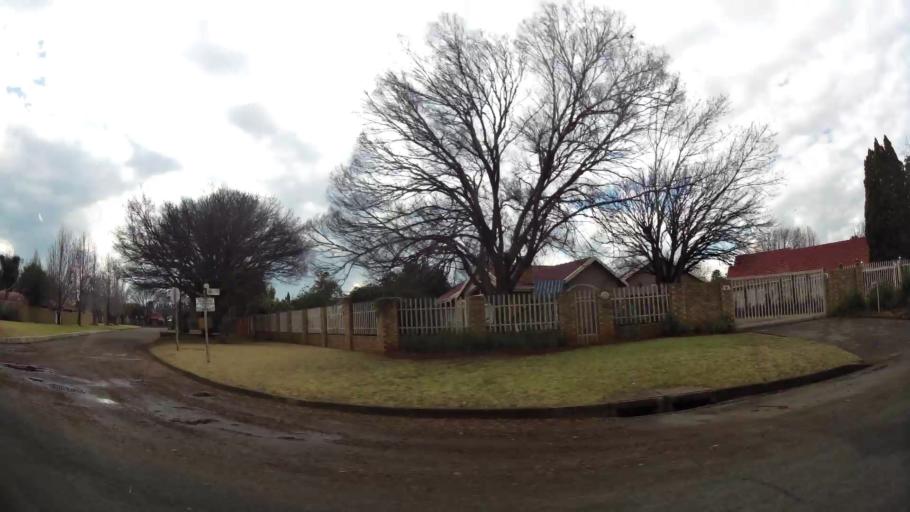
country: ZA
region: Gauteng
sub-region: Sedibeng District Municipality
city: Vereeniging
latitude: -26.6402
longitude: 27.9790
